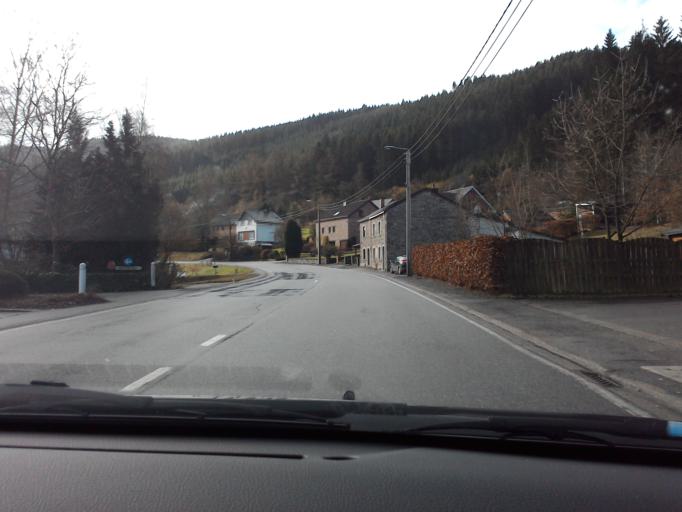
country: BE
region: Wallonia
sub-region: Province de Liege
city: Trois-Ponts
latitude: 50.3634
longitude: 5.8739
